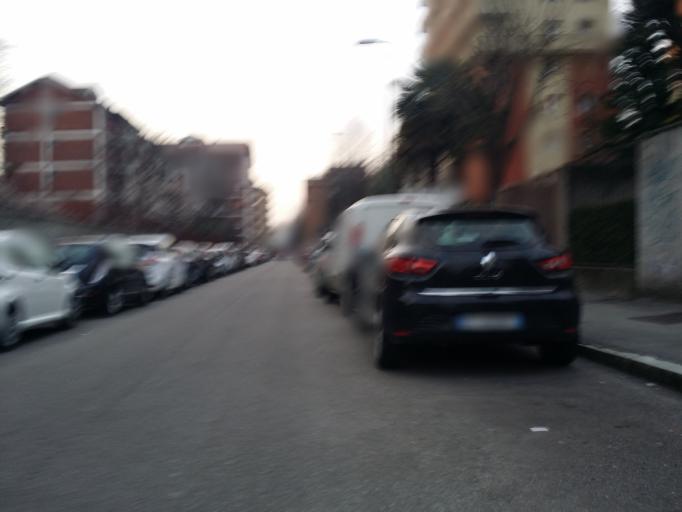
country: IT
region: Lombardy
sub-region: Citta metropolitana di Milano
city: Romano Banco
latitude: 45.4560
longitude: 9.1215
